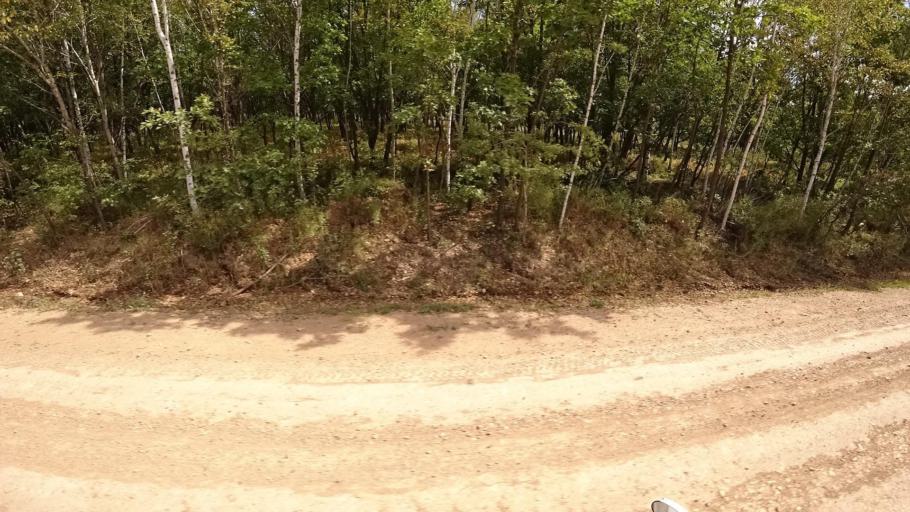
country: RU
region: Primorskiy
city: Yakovlevka
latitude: 44.7298
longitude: 133.6095
